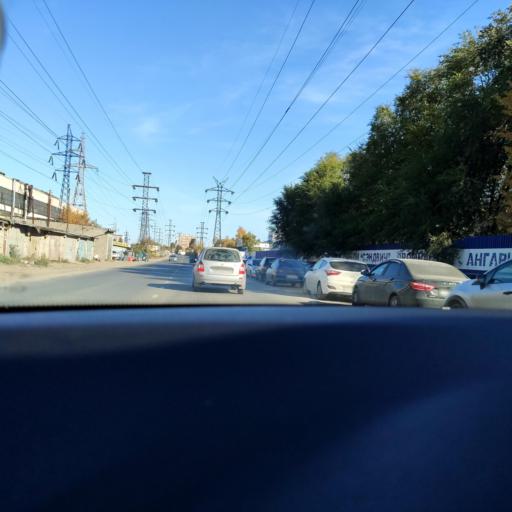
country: RU
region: Samara
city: Petra-Dubrava
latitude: 53.2415
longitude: 50.2899
